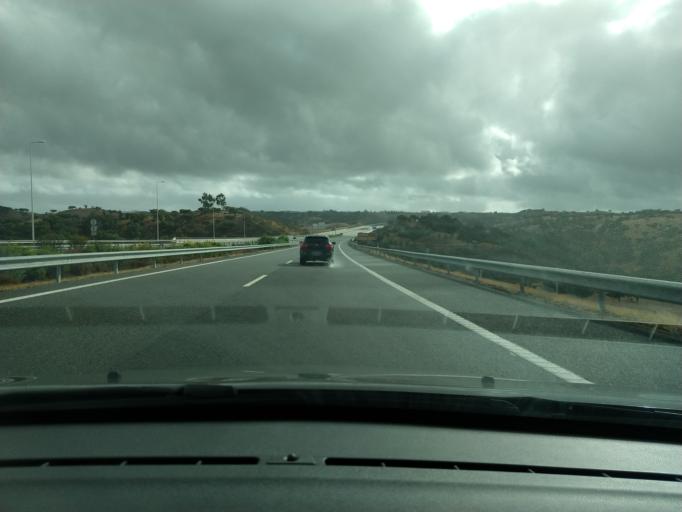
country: PT
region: Beja
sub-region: Almodovar
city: Almodovar
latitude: 37.5181
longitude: -8.1827
